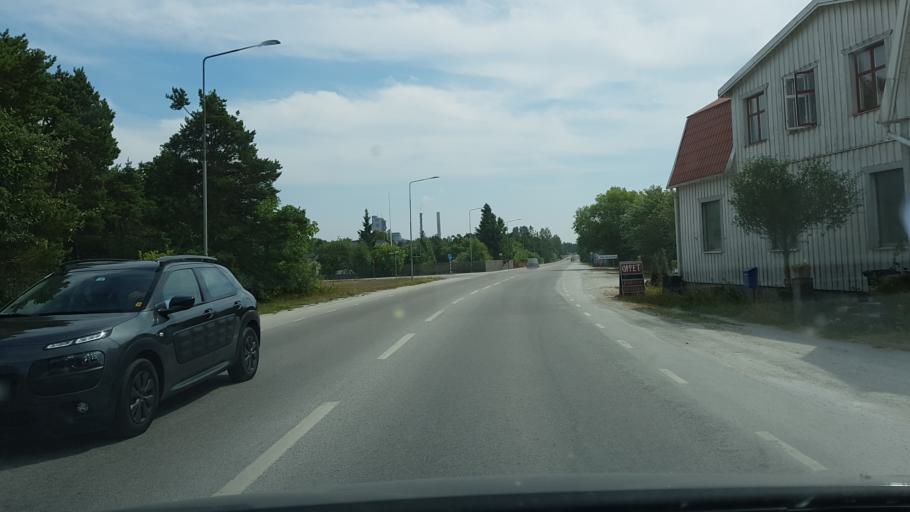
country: SE
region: Gotland
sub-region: Gotland
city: Slite
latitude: 57.7209
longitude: 18.7906
